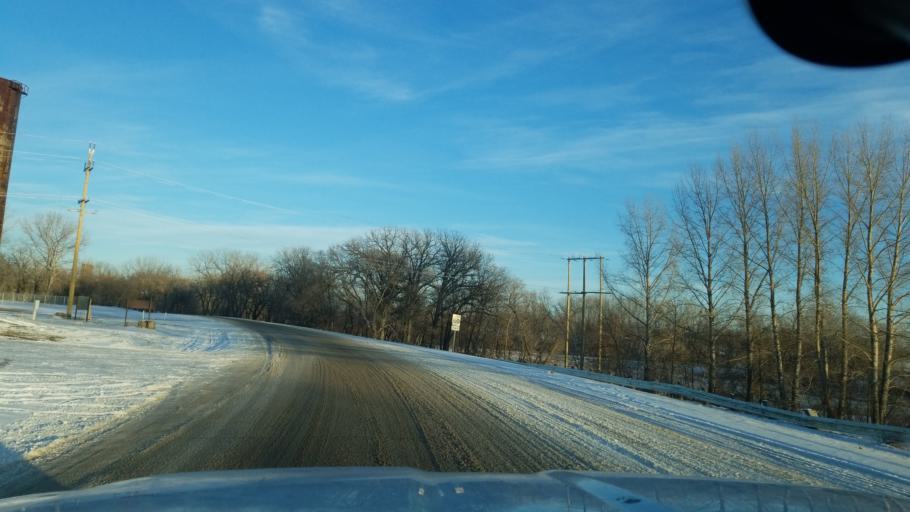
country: CA
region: Manitoba
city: Portage la Prairie
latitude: 49.9492
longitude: -98.3317
